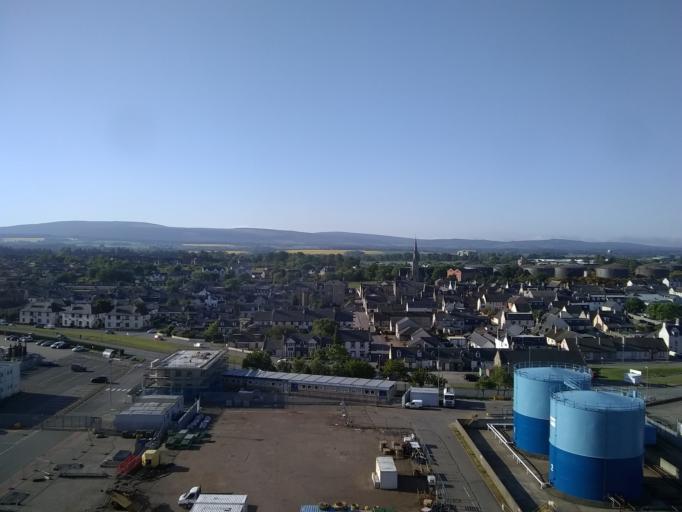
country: GB
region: Scotland
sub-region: Highland
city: Invergordon
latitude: 57.6850
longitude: -4.1691
